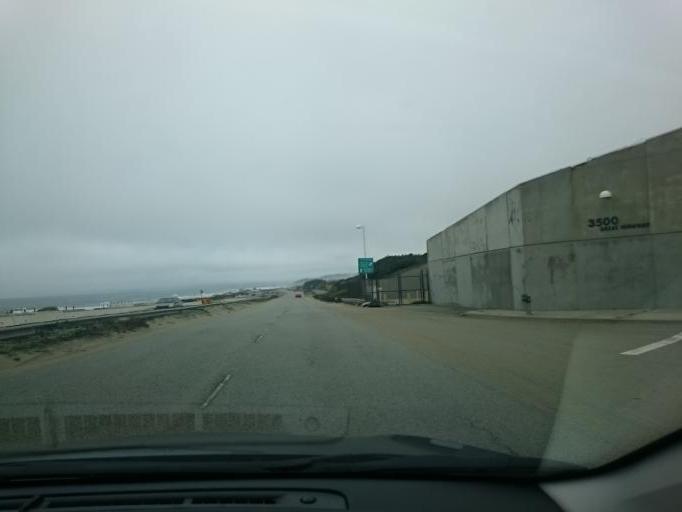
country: US
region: California
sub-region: San Mateo County
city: Broadmoor
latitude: 37.7280
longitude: -122.5062
